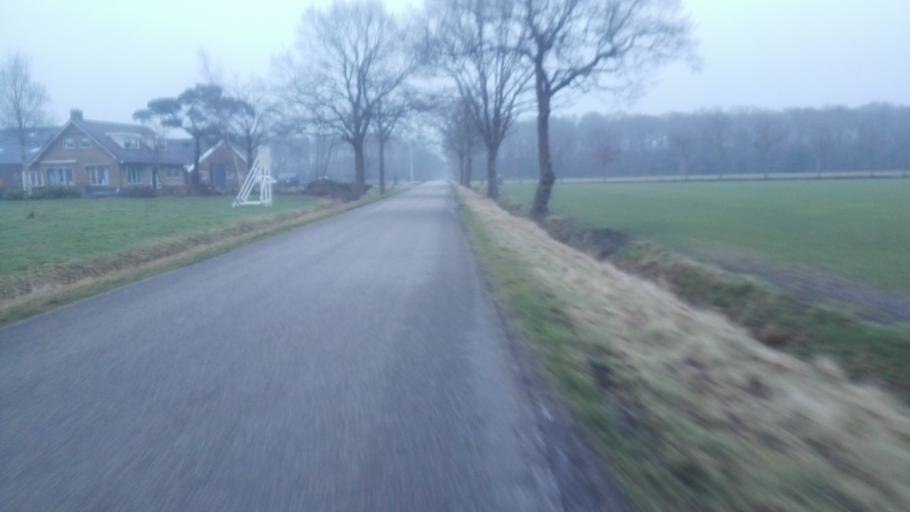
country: NL
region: Friesland
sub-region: Gemeente Weststellingwerf
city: Noordwolde
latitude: 52.9499
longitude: 6.1526
